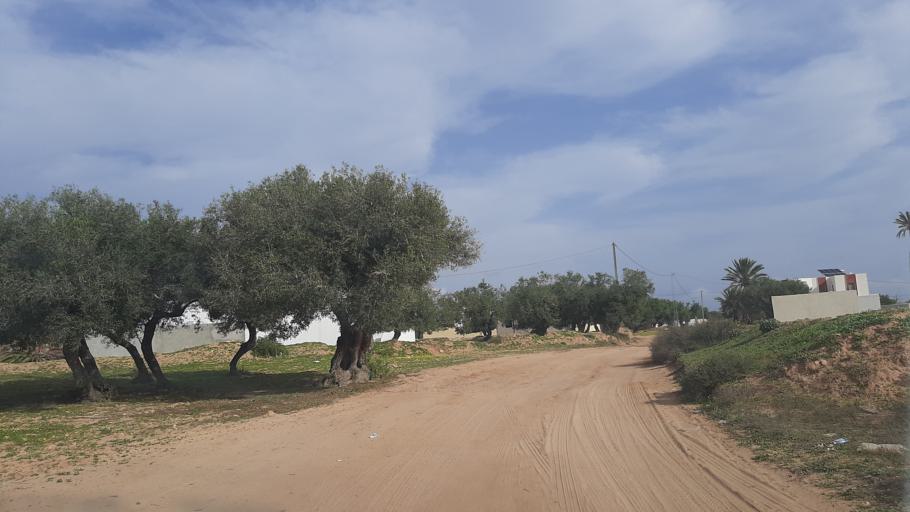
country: TN
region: Madanin
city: Midoun
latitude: 33.8094
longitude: 11.0245
